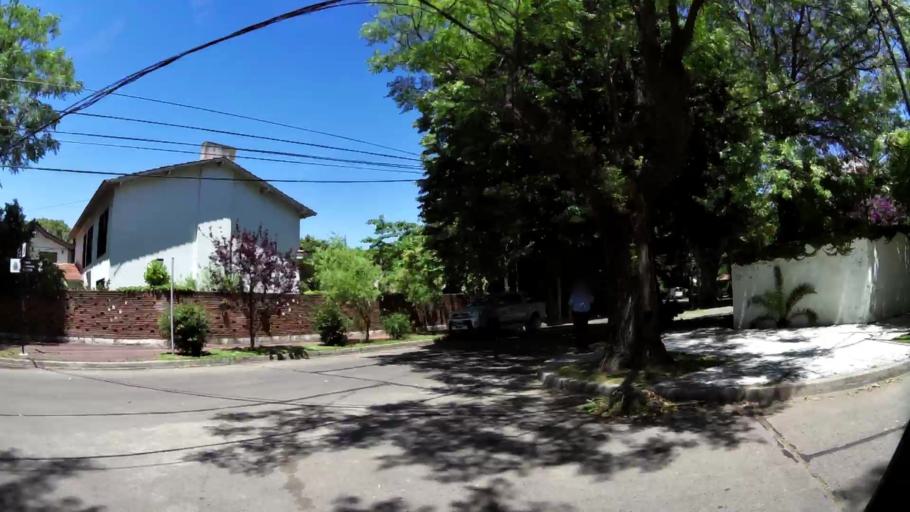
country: AR
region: Buenos Aires
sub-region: Partido de San Isidro
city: San Isidro
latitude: -34.4754
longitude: -58.5037
